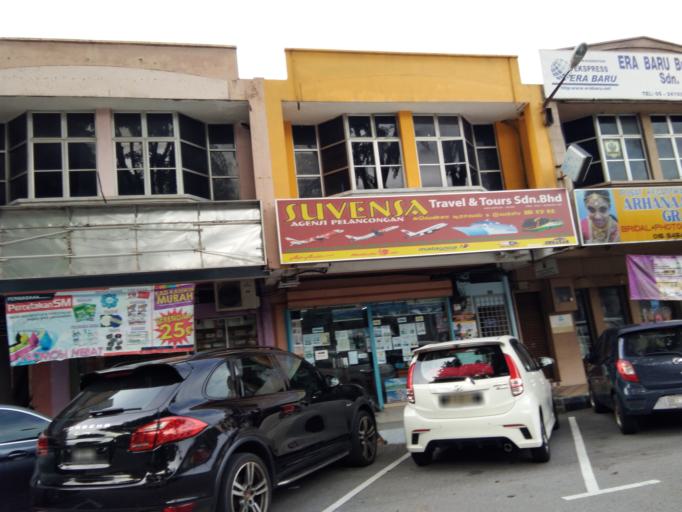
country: MY
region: Perak
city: Ipoh
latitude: 4.6080
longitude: 101.0816
